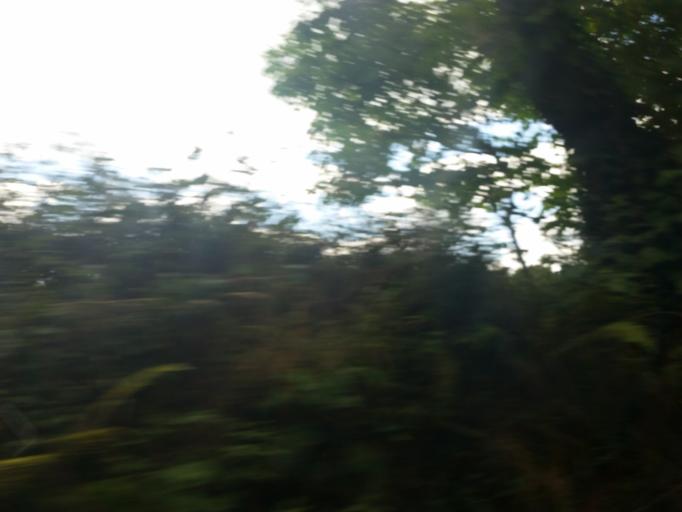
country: IE
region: Munster
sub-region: Waterford
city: Portlaw
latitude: 52.1764
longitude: -7.3673
